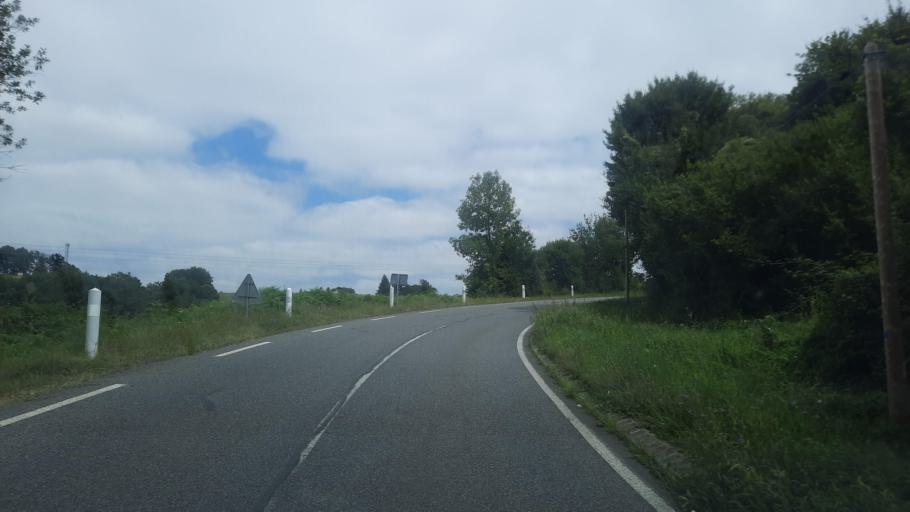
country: FR
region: Midi-Pyrenees
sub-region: Departement des Hautes-Pyrenees
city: Trie-sur-Baise
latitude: 43.3037
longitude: 0.3870
